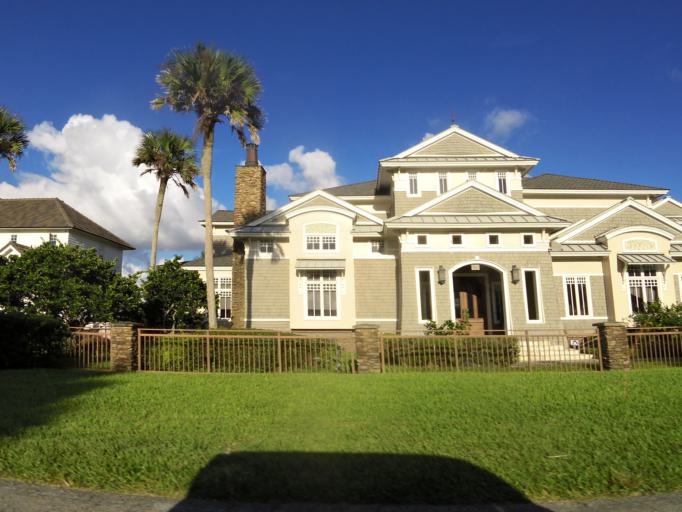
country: US
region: Florida
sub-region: Saint Johns County
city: Sawgrass
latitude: 30.2047
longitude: -81.3682
